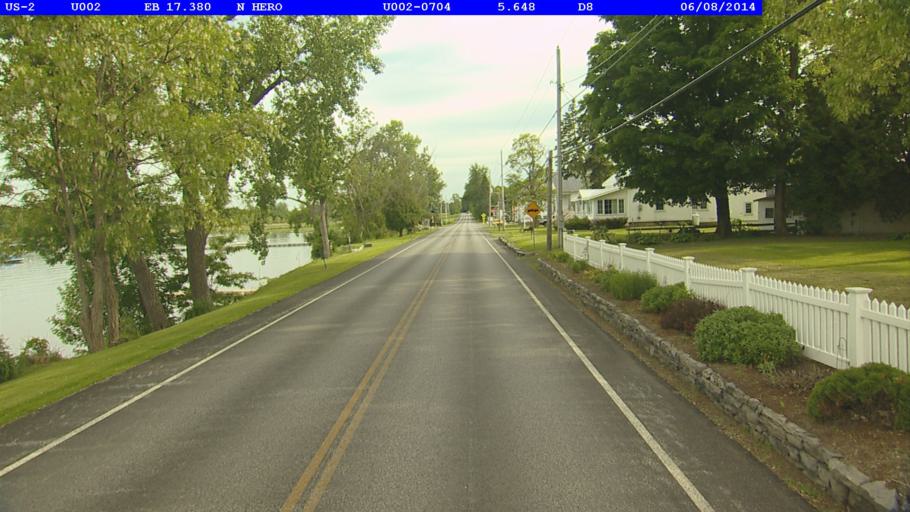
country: US
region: Vermont
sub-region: Grand Isle County
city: North Hero
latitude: 44.8177
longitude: -73.2898
